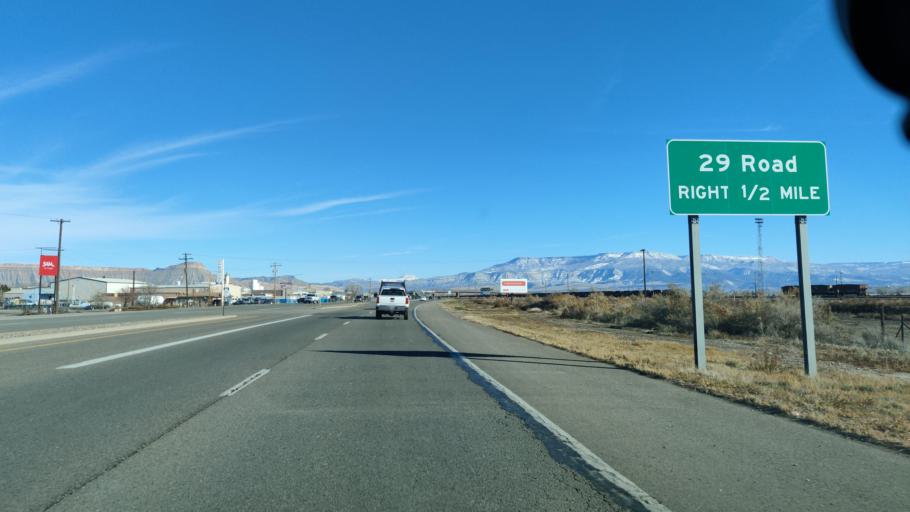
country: US
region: Colorado
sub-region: Mesa County
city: Grand Junction
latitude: 39.0693
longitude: -108.5284
